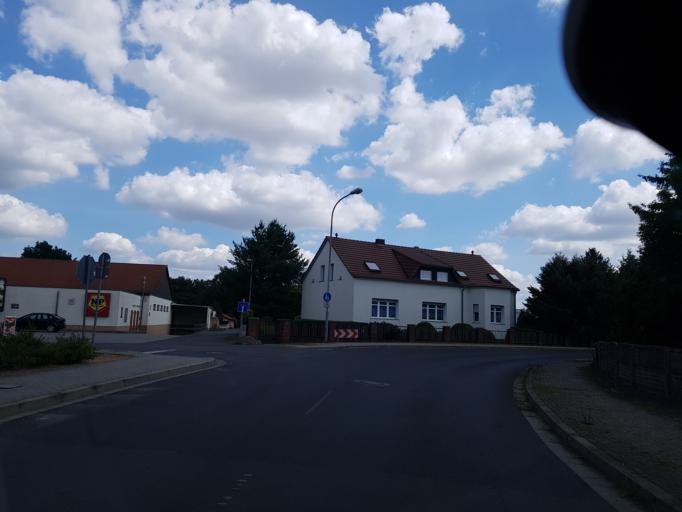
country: DE
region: Brandenburg
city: Drebkau
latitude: 51.6555
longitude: 14.2256
